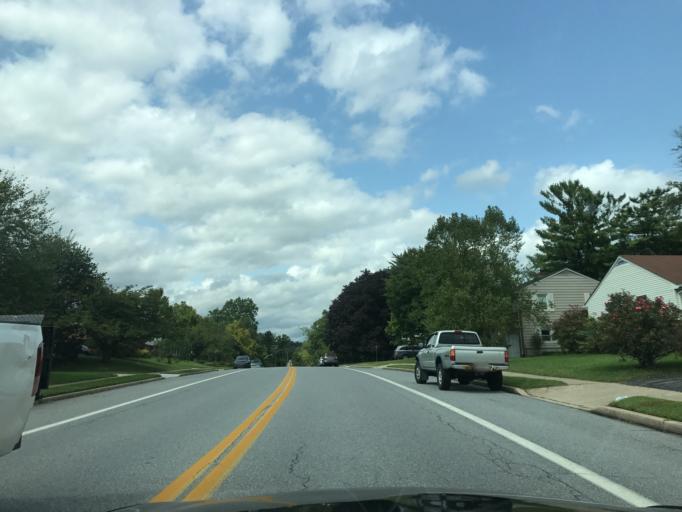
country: US
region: Maryland
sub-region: Baltimore County
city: Mays Chapel
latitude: 39.4160
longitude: -76.6468
